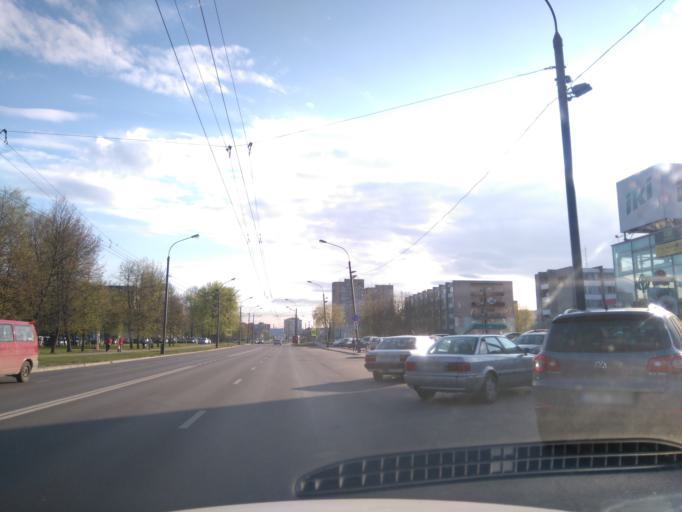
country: LT
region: Kauno apskritis
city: Dainava (Kaunas)
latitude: 54.9206
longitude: 23.9741
